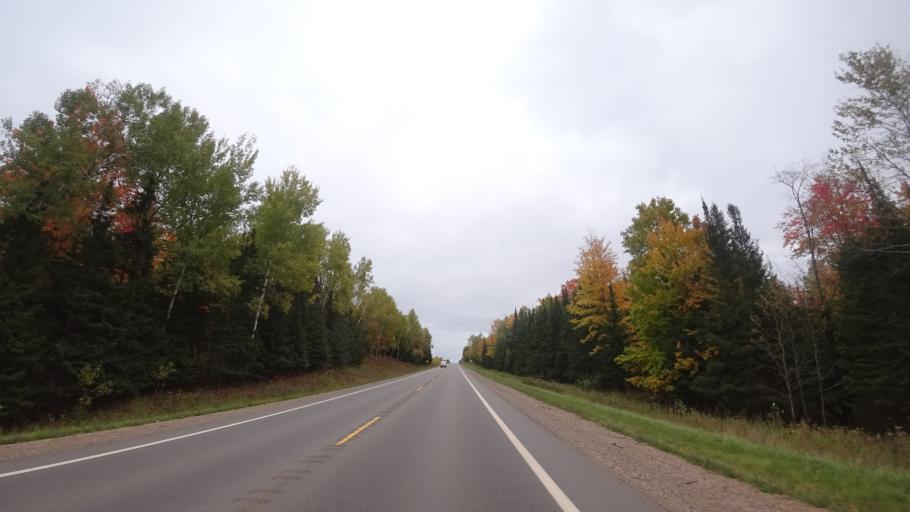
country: US
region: Michigan
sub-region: Iron County
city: Crystal Falls
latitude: 46.1790
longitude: -88.0468
